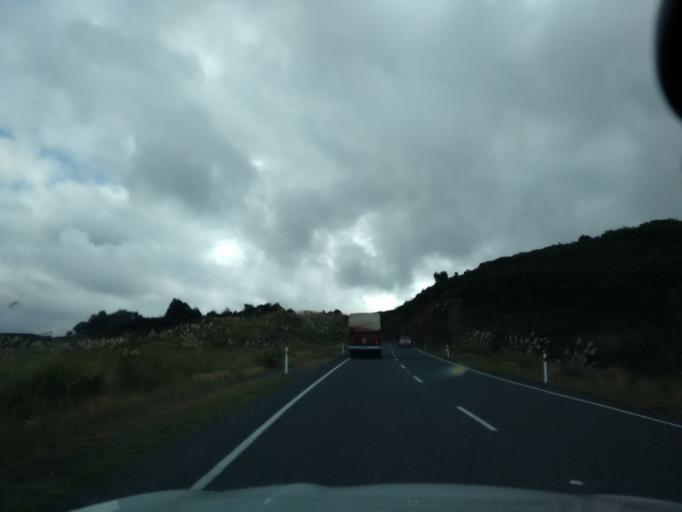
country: NZ
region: Waikato
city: Turangi
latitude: -39.0567
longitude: 175.5841
